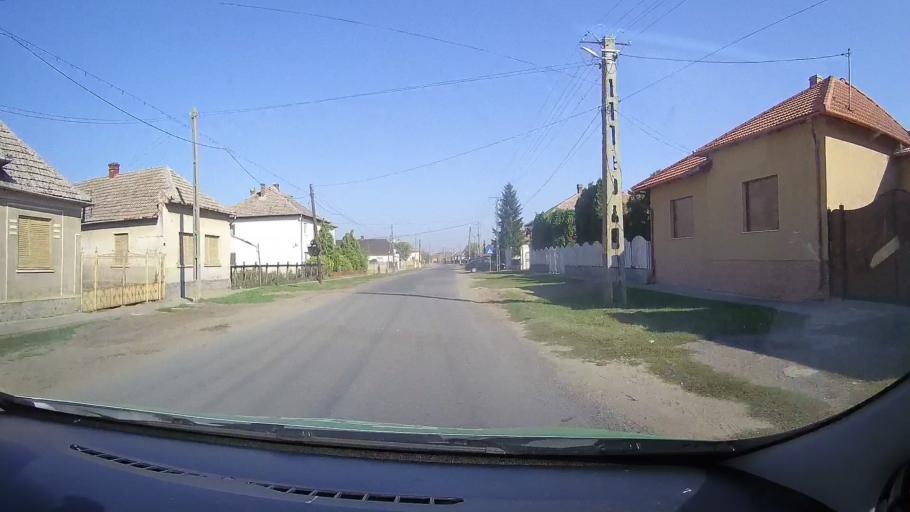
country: RO
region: Satu Mare
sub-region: Comuna Ciumesti
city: Ciumesti
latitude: 47.6608
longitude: 22.3351
